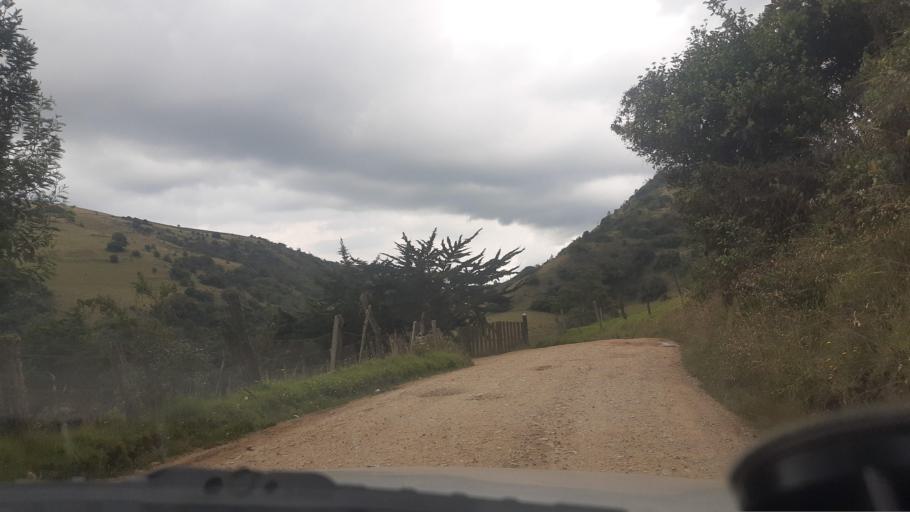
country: CO
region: Cundinamarca
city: Suesca
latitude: 5.1301
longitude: -73.7868
